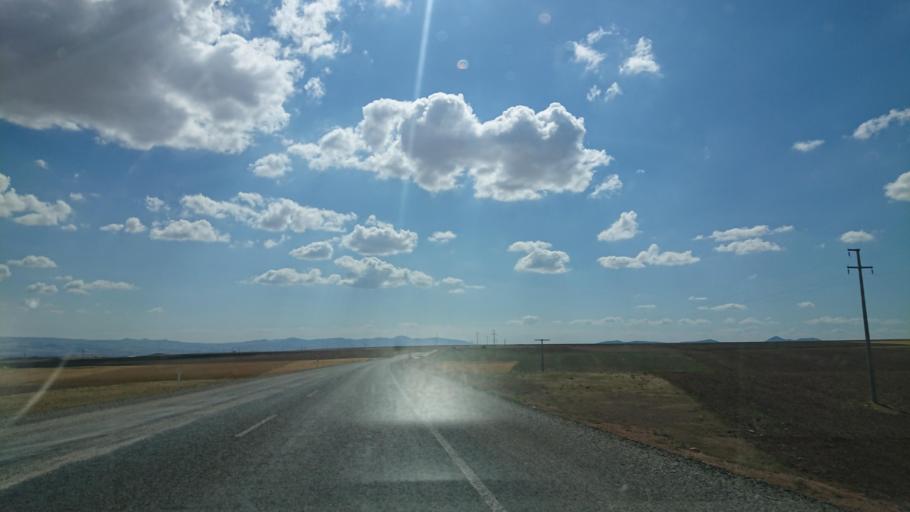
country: TR
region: Kirsehir
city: Kirsehir
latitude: 39.1231
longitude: 34.0227
